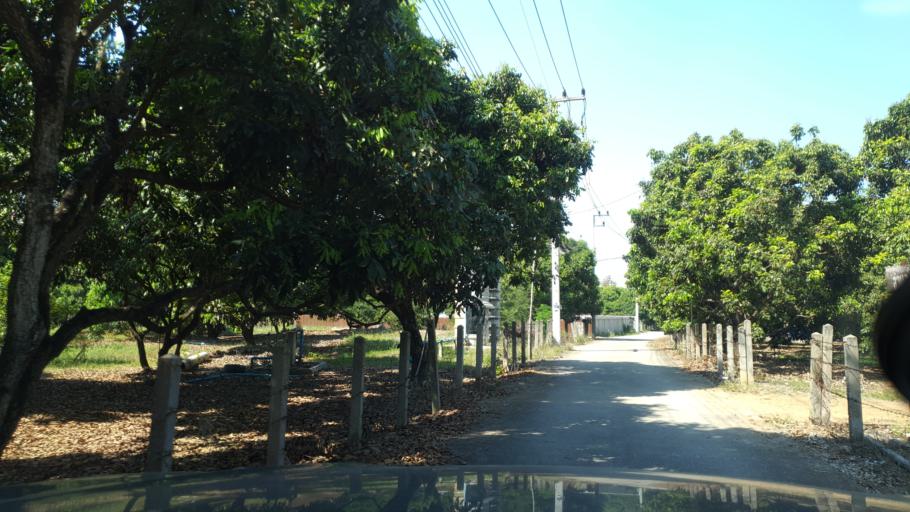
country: TH
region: Chiang Mai
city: Mae On
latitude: 18.7211
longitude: 99.1943
